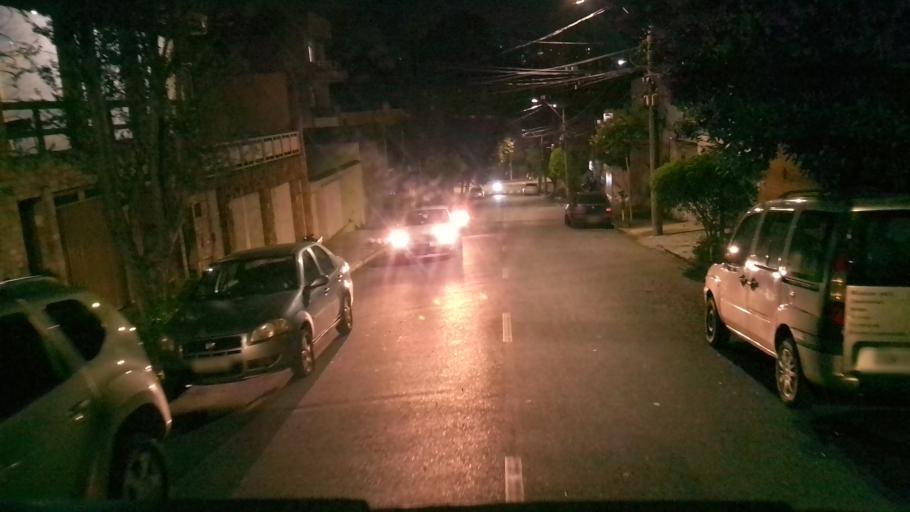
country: BR
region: Minas Gerais
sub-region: Belo Horizonte
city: Belo Horizonte
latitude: -19.9108
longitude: -43.9152
